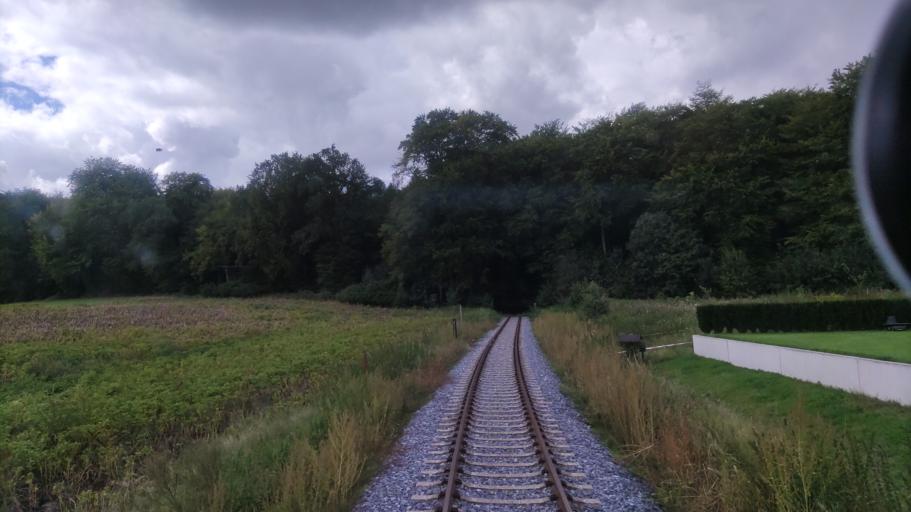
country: DE
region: Lower Saxony
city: Scharnebeck
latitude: 53.2830
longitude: 10.4995
